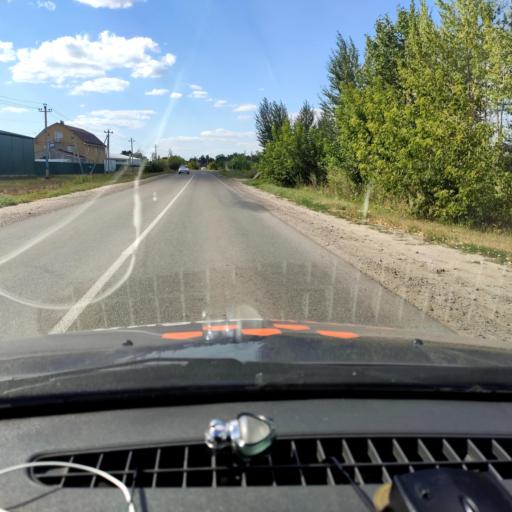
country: RU
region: Voronezj
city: Somovo
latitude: 51.6977
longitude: 39.3775
